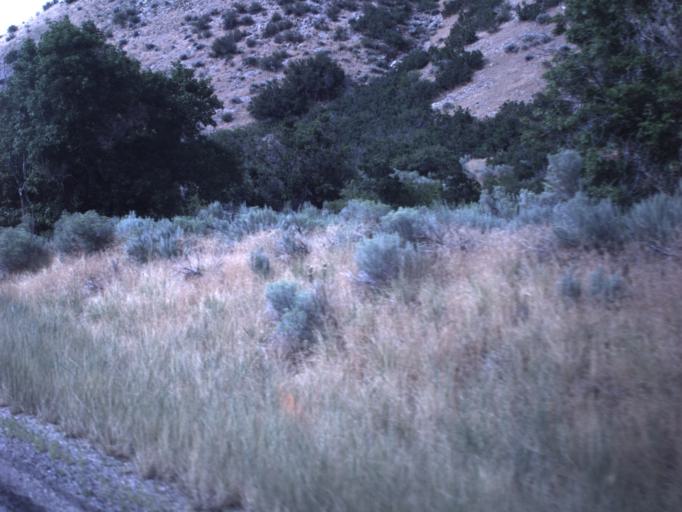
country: US
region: Utah
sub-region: Wasatch County
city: Heber
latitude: 40.4281
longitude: -111.3491
